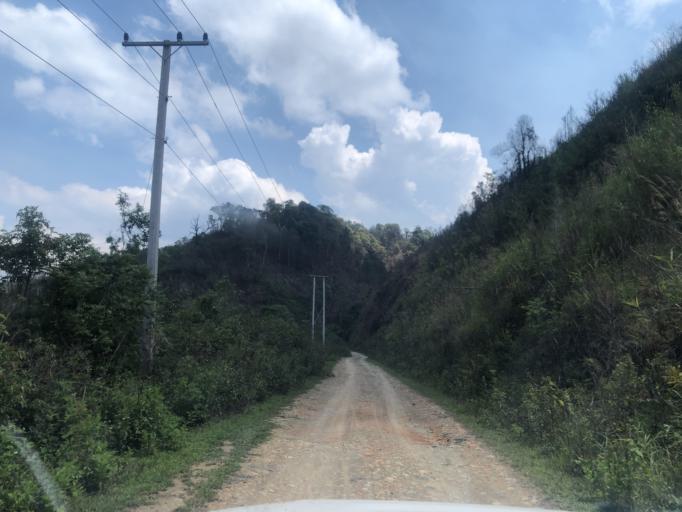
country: LA
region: Phongsali
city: Phongsali
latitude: 21.3998
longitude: 102.1894
